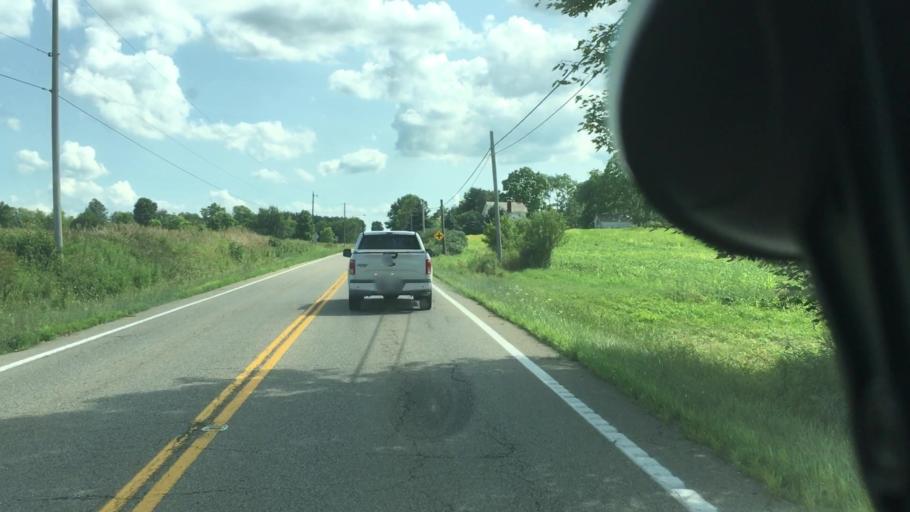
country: US
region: Ohio
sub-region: Columbiana County
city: Salem
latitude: 40.9752
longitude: -80.8277
